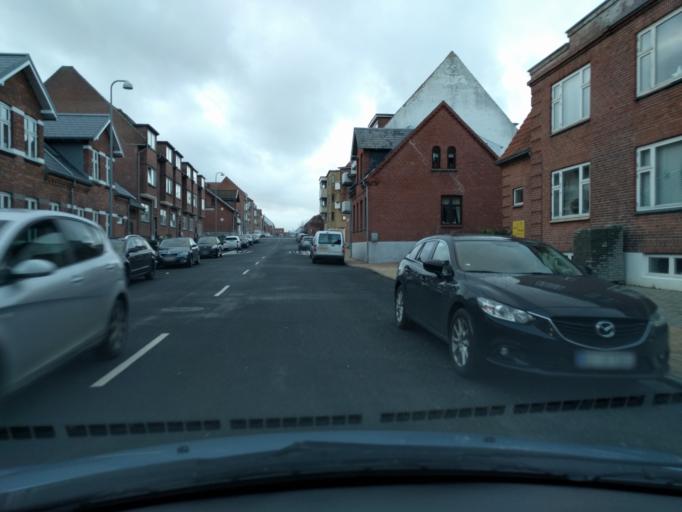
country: DK
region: South Denmark
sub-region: Odense Kommune
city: Odense
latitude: 55.4078
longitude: 10.4001
